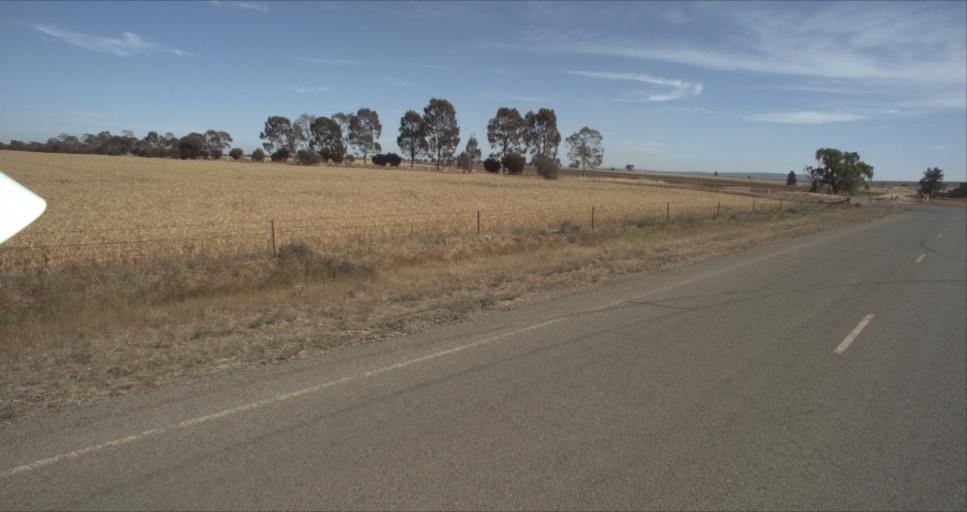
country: AU
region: New South Wales
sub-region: Leeton
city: Leeton
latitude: -34.5613
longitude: 146.4817
